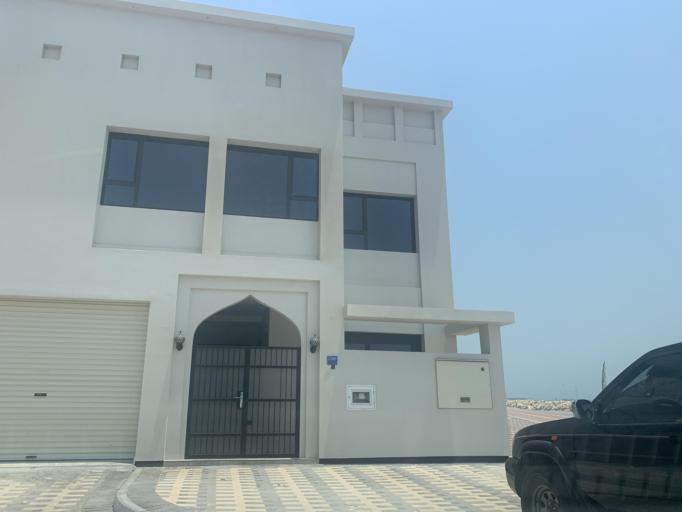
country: BH
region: Muharraq
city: Al Hadd
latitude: 26.2314
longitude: 50.6732
